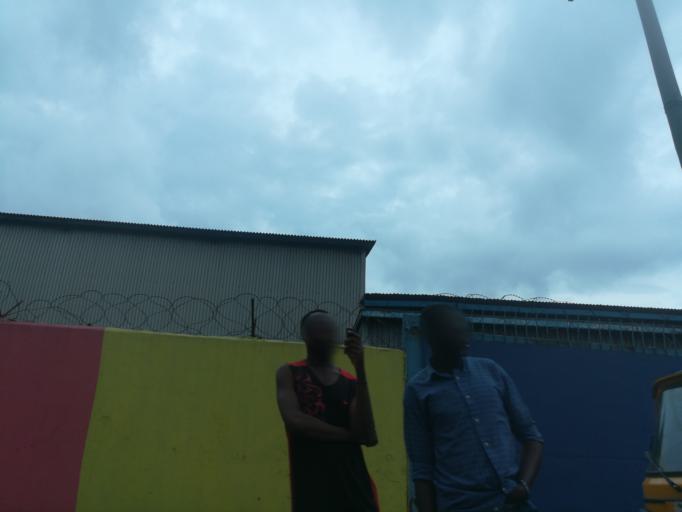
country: NG
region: Lagos
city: Agege
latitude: 6.6146
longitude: 3.3363
